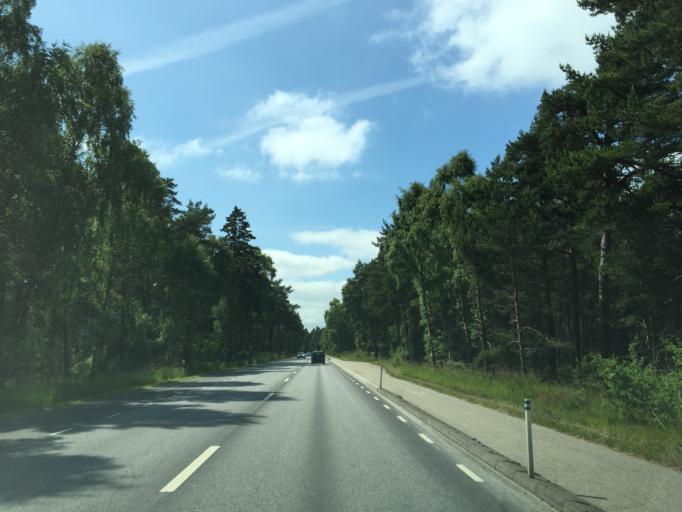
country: SE
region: Skane
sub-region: Ystads Kommun
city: Kopingebro
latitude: 55.4364
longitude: 13.8957
